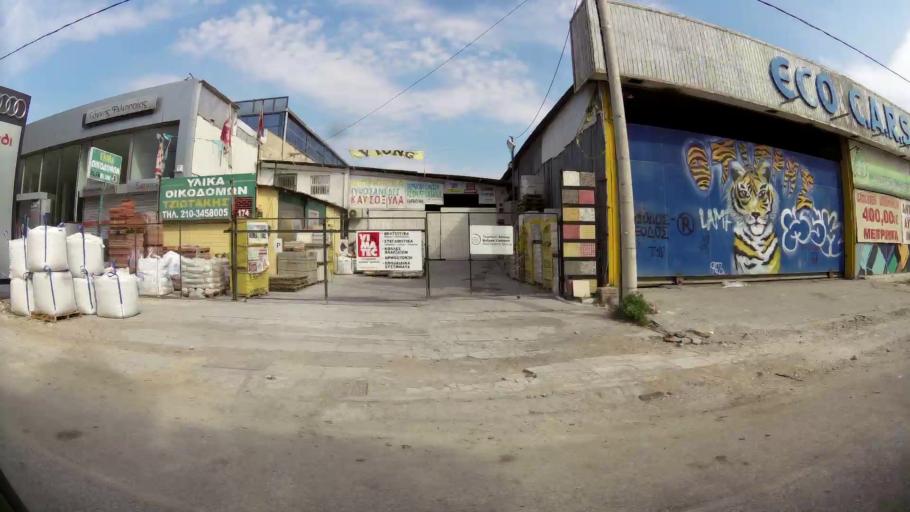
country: GR
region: Attica
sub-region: Nomarchia Athinas
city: Aigaleo
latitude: 37.9894
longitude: 23.6887
